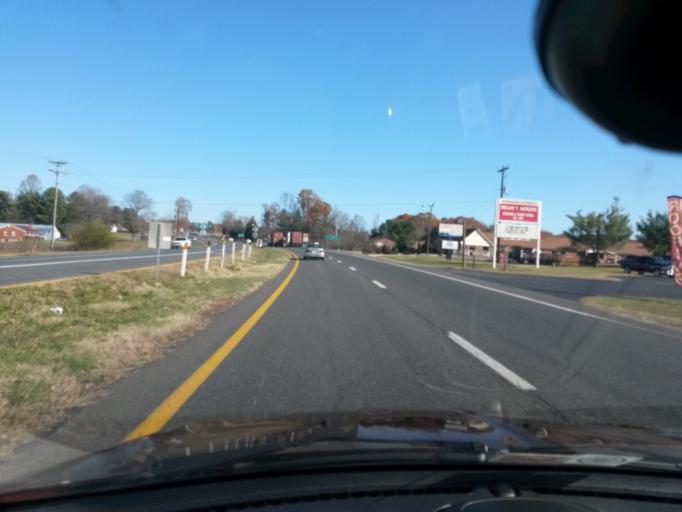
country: US
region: Virginia
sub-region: Campbell County
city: Timberlake
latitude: 37.3059
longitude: -79.2721
